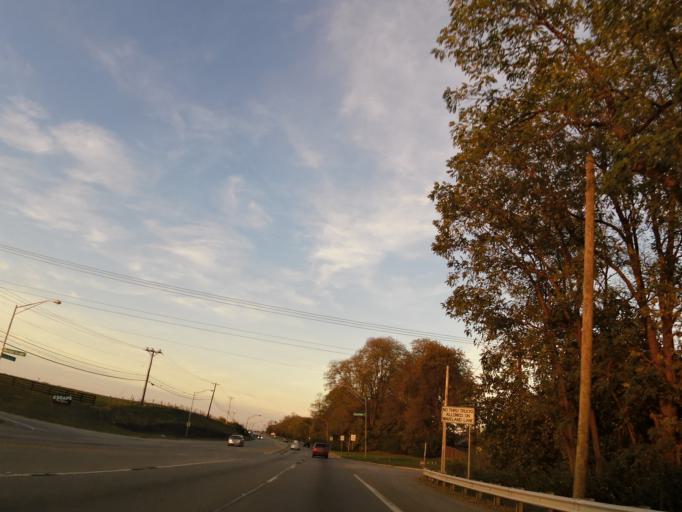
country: US
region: Kentucky
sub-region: Fayette County
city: Monticello
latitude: 37.9691
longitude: -84.5332
